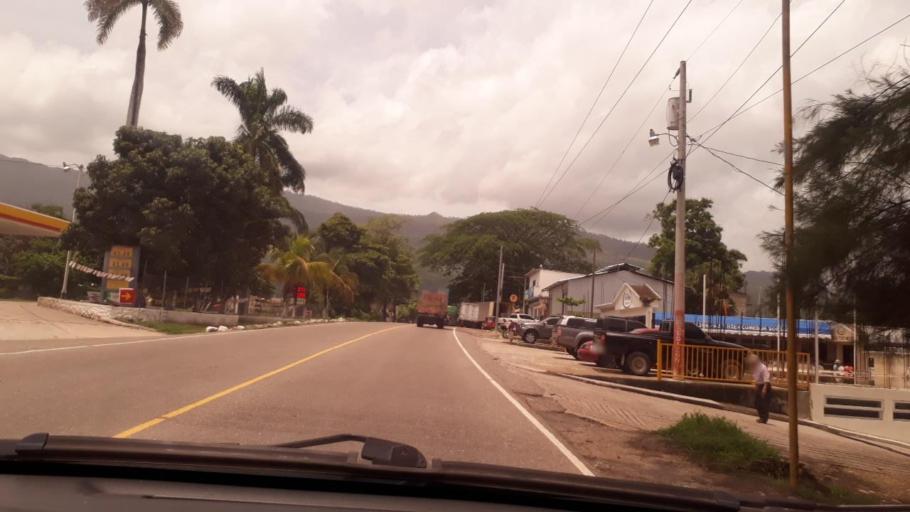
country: GT
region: Chiquimula
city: Quezaltepeque
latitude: 14.6346
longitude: -89.4451
